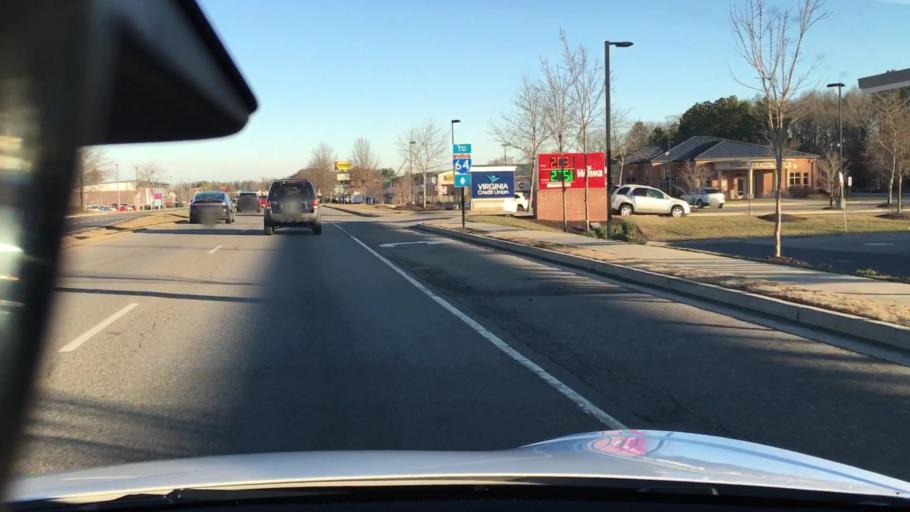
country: US
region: Virginia
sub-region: Henrico County
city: Fort Lee
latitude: 37.5121
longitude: -77.3495
